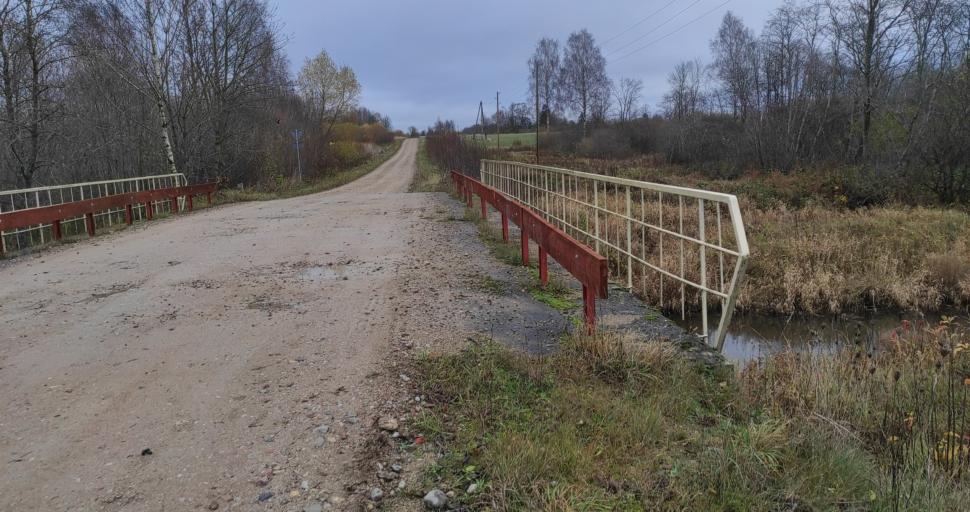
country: LV
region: Priekule
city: Priekule
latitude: 56.5031
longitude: 21.4894
